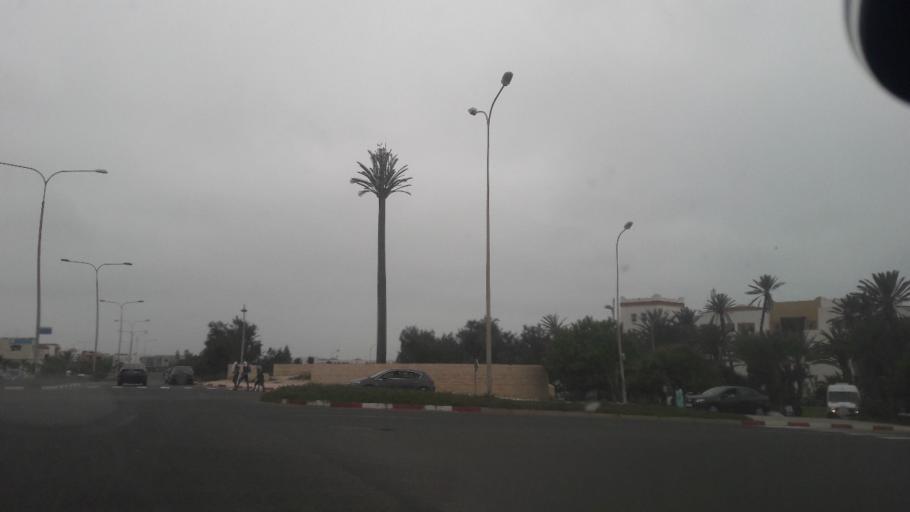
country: MA
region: Souss-Massa-Draa
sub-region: Agadir-Ida-ou-Tnan
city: Agadir
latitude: 30.3959
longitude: -9.5951
